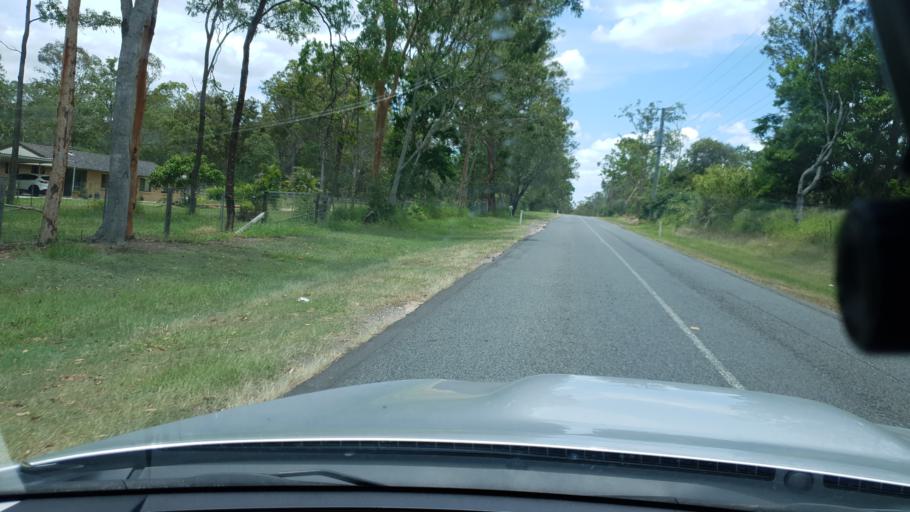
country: AU
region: Queensland
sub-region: Logan
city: North Maclean
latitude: -27.7721
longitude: 152.9906
